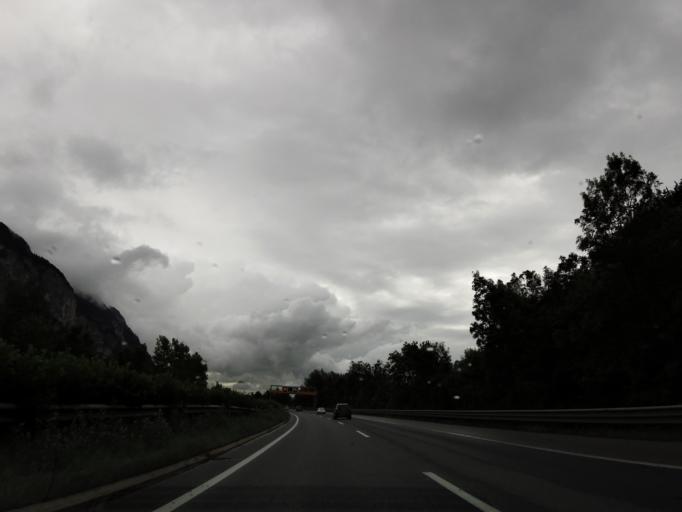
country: AT
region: Tyrol
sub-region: Politischer Bezirk Innsbruck Land
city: Unterperfuss
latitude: 47.2616
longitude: 11.2443
